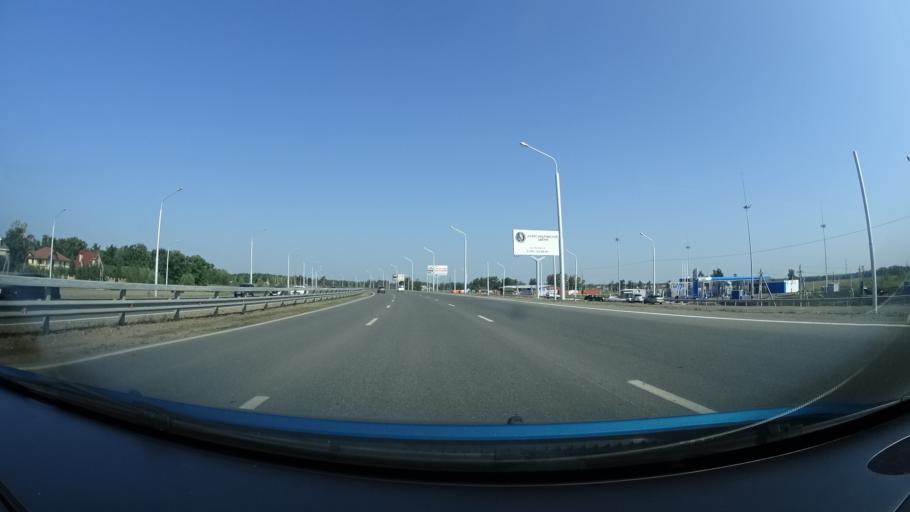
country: RU
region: Bashkortostan
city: Ufa
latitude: 54.7731
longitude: 55.9536
